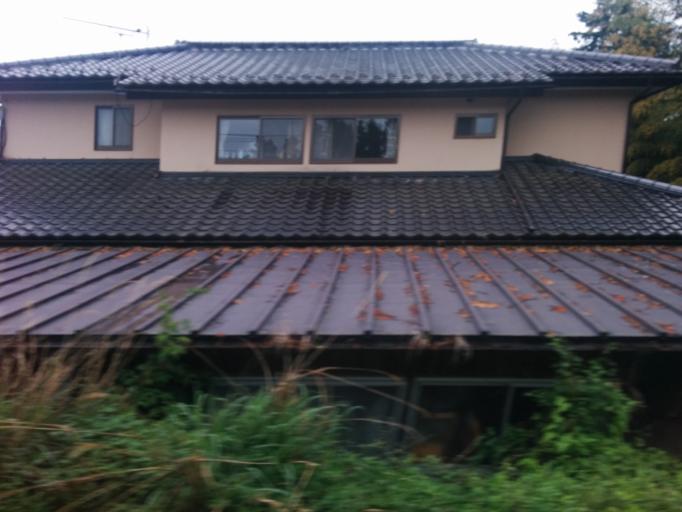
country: JP
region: Tochigi
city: Imaichi
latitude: 36.7332
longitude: 139.6525
